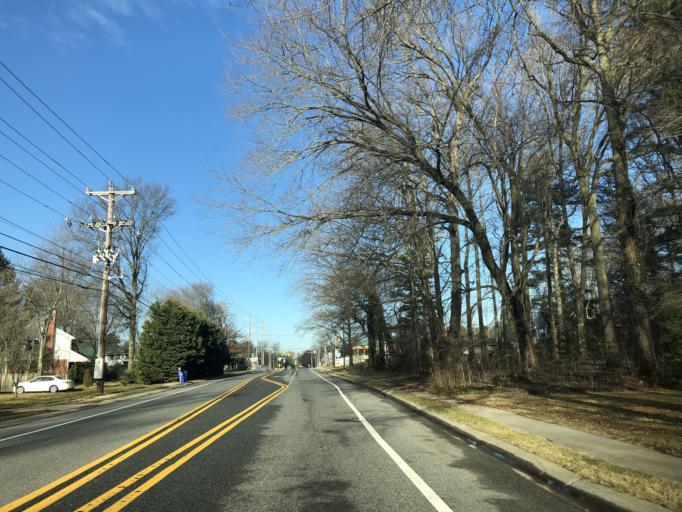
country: US
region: Delaware
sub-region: New Castle County
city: Bellefonte
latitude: 39.8070
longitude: -75.5130
